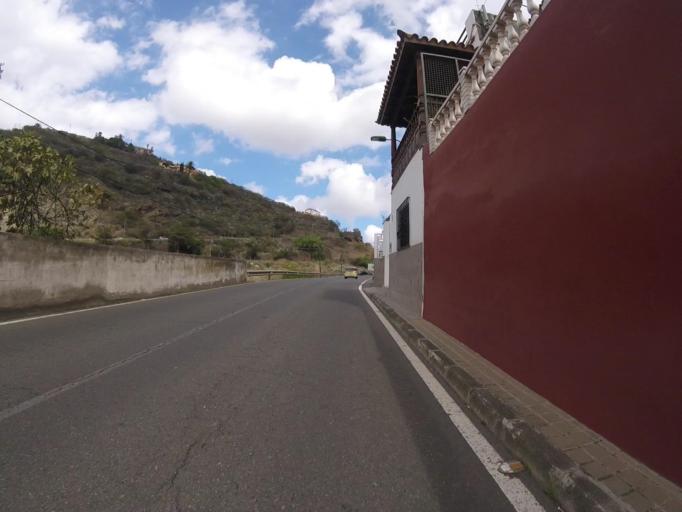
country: ES
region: Canary Islands
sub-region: Provincia de Las Palmas
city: Santa Brigida
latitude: 28.0539
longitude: -15.4777
